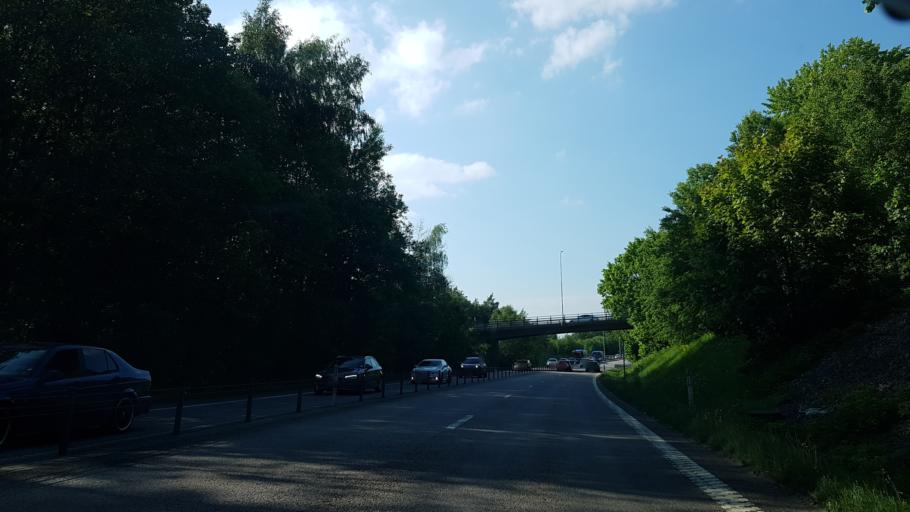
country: SE
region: Vaestra Goetaland
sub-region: Goteborg
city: Billdal
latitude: 57.6126
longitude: 11.9425
